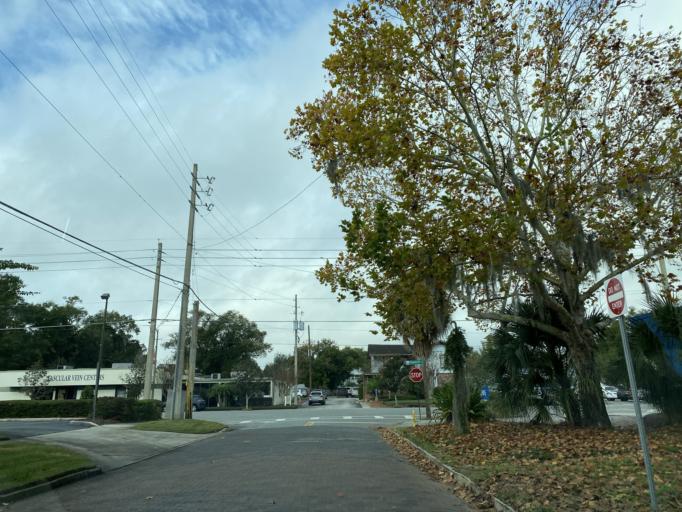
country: US
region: Florida
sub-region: Orange County
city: Orlando
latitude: 28.5626
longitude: -81.3888
